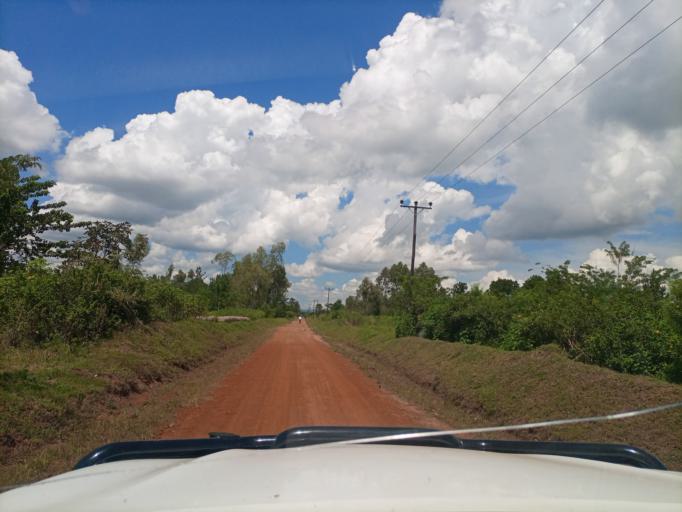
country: UG
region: Eastern Region
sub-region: Tororo District
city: Tororo
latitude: 0.6541
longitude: 33.9984
